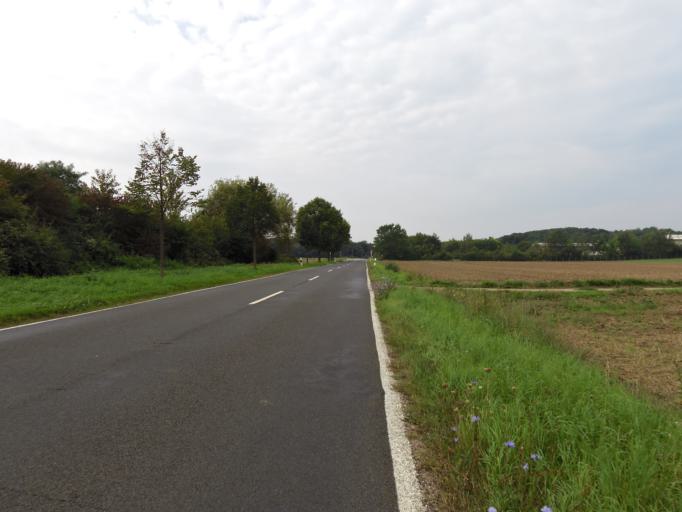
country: DE
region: Rheinland-Pfalz
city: Siefersheim
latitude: 49.7782
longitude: 7.9407
